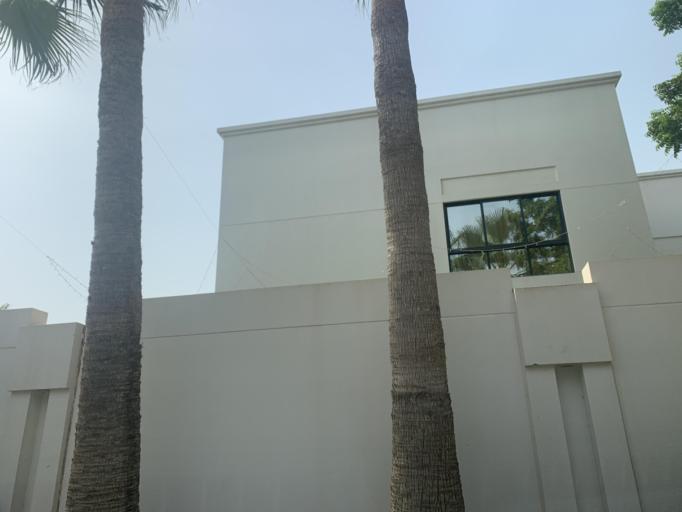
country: BH
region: Manama
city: Jidd Hafs
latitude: 26.2022
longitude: 50.4794
